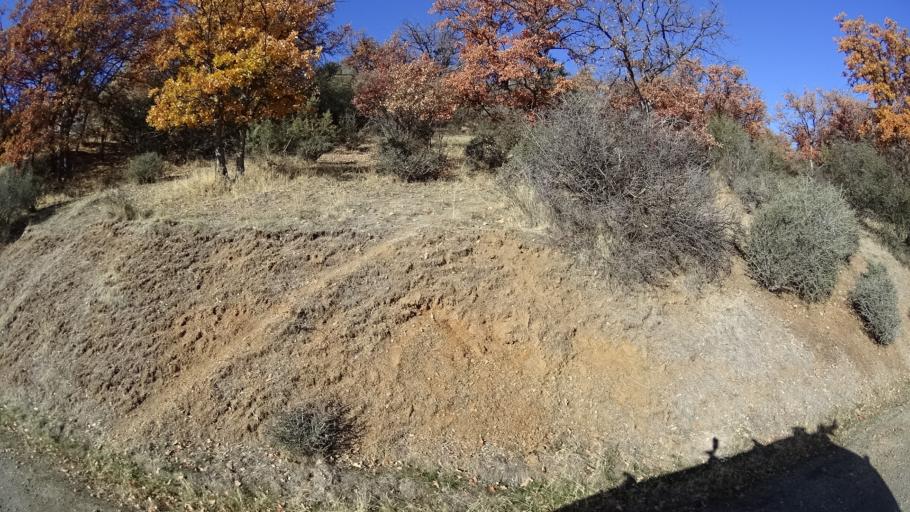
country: US
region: California
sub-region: Siskiyou County
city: Yreka
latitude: 41.6949
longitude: -122.6512
